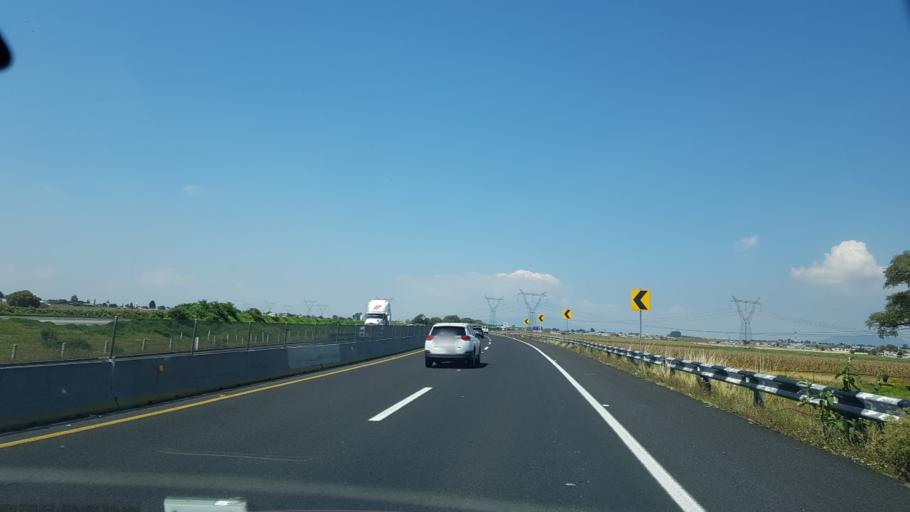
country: MX
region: Mexico
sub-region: Otzolotepec
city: La Y
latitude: 19.3986
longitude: -99.5776
